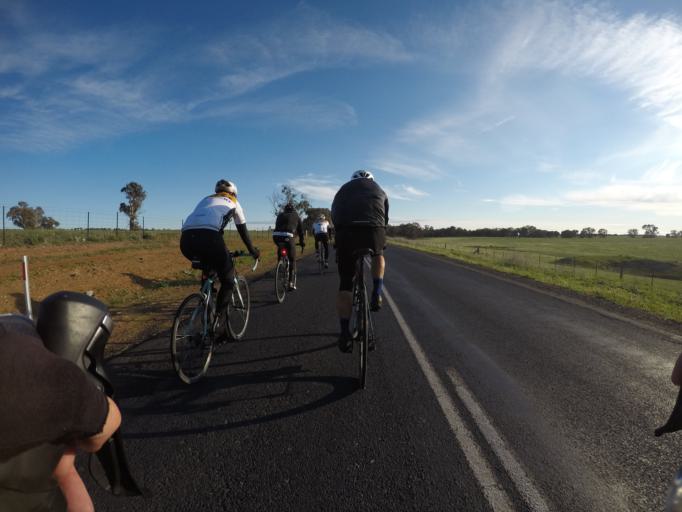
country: AU
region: New South Wales
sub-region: Cabonne
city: Molong
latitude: -32.9974
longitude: 148.7869
